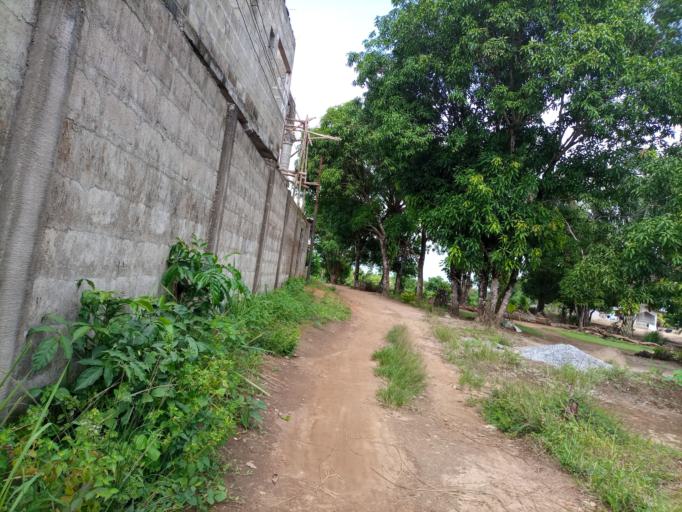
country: SL
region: Southern Province
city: Bo
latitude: 7.9694
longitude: -11.7643
